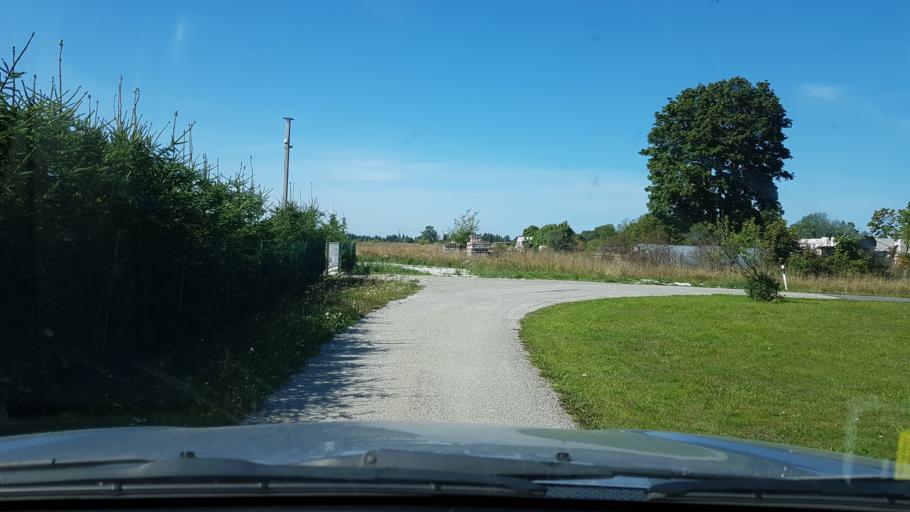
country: EE
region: Ida-Virumaa
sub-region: Sillamaee linn
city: Sillamae
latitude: 59.3809
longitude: 27.8181
